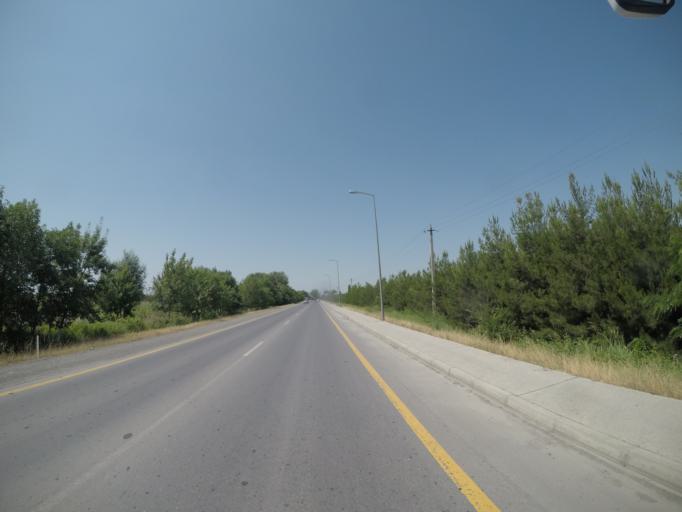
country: AZ
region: Agdas
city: Agdas
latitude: 40.6401
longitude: 47.4907
